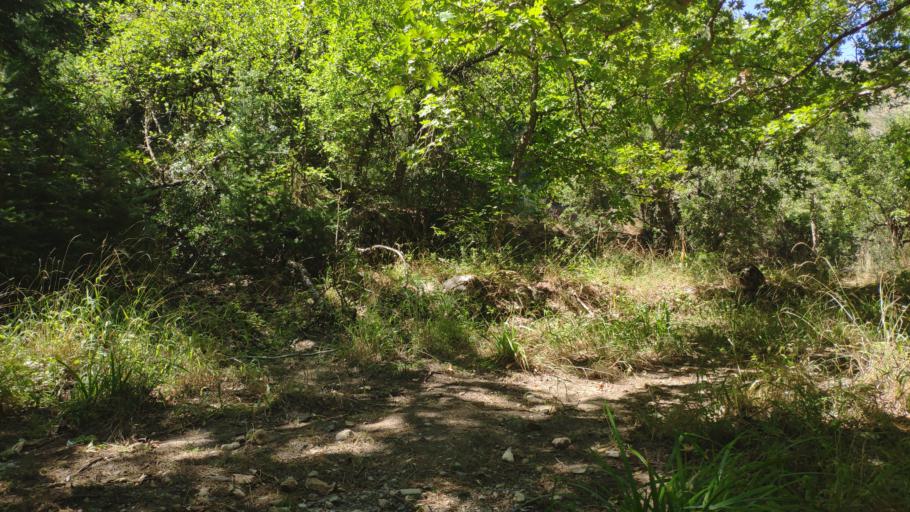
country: GR
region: Peloponnese
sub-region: Nomos Lakonias
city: Kariai
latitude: 37.1759
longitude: 22.5896
